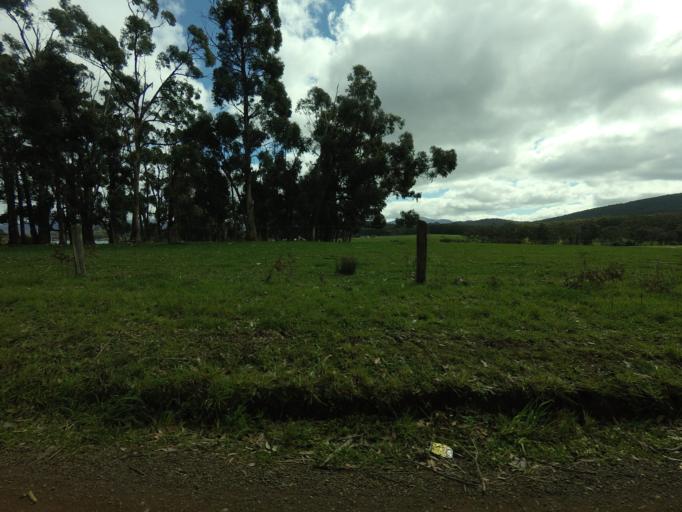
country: AU
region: Tasmania
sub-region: Huon Valley
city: Geeveston
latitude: -43.4347
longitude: 146.9868
